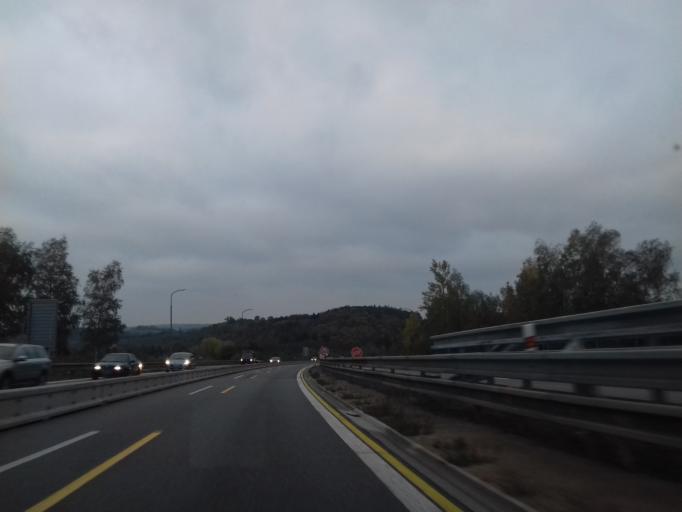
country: CZ
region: Central Bohemia
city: Trhovy Stepanov
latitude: 49.7523
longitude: 15.0231
